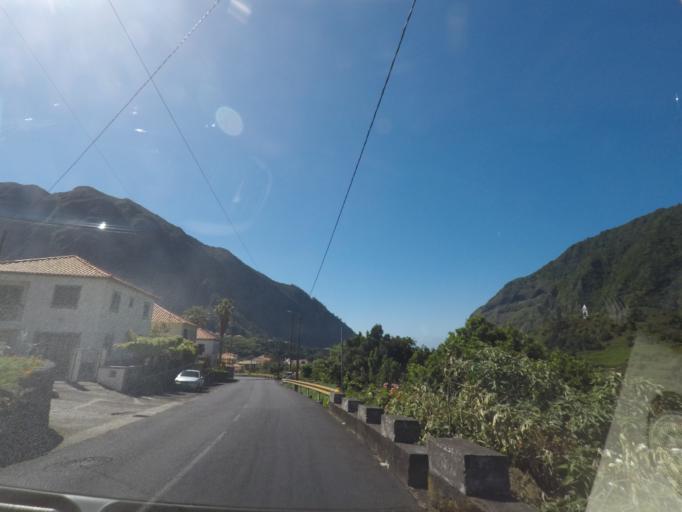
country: PT
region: Madeira
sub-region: Sao Vicente
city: Sao Vicente
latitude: 32.7908
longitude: -17.0366
